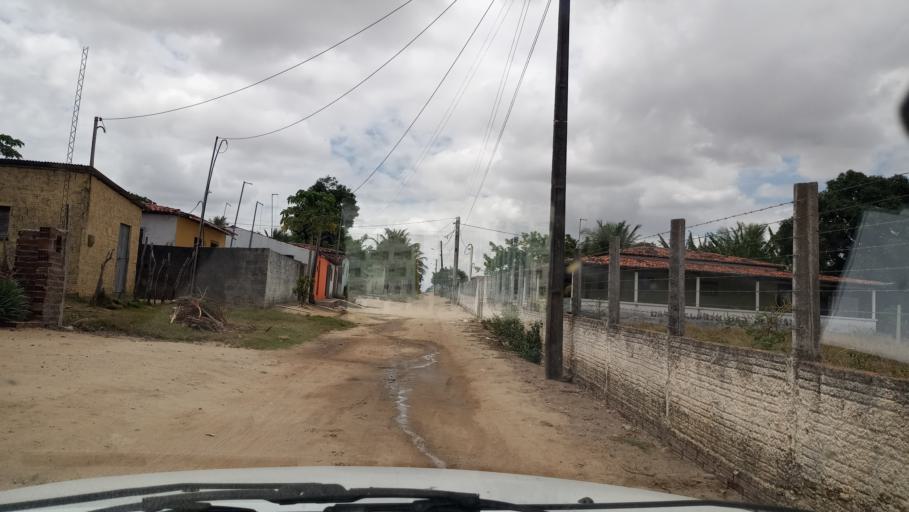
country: BR
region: Rio Grande do Norte
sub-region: Santo Antonio
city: Santo Antonio
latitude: -6.2108
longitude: -35.4674
